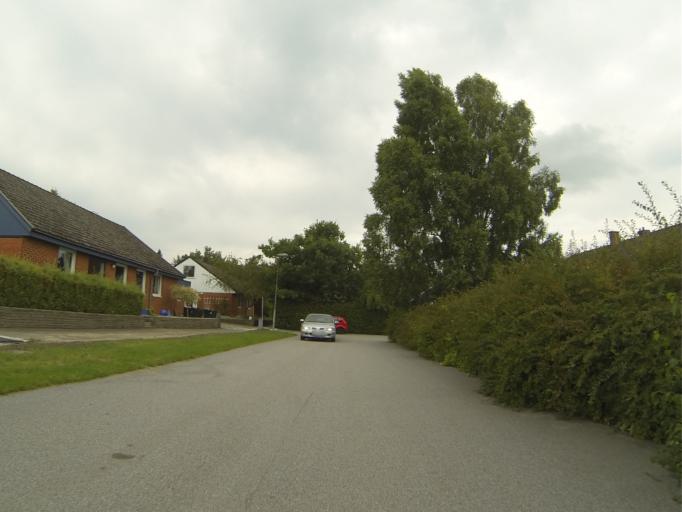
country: SE
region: Skane
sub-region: Eslovs Kommun
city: Eslov
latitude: 55.7240
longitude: 13.3367
